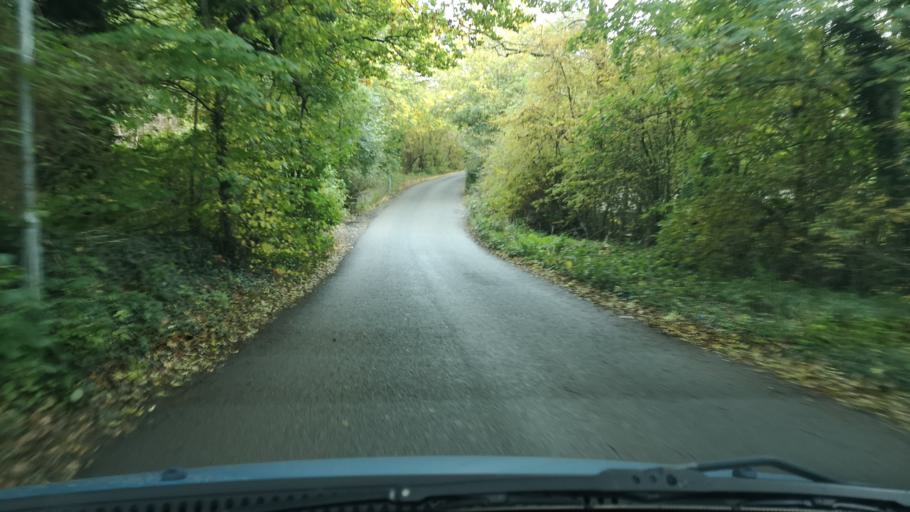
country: GB
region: England
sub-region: City and Borough of Leeds
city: Drighlington
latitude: 53.7377
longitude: -1.6750
